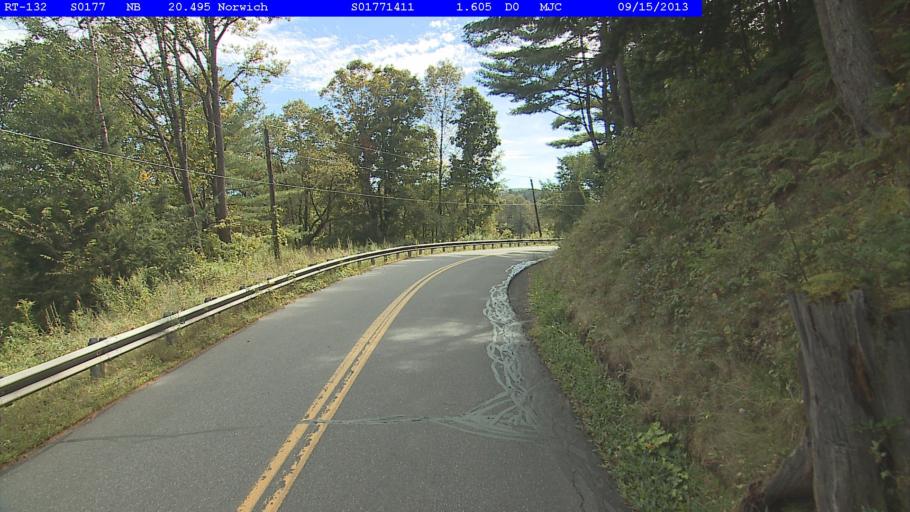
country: US
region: New Hampshire
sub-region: Grafton County
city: Hanover
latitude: 43.7679
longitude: -72.2465
